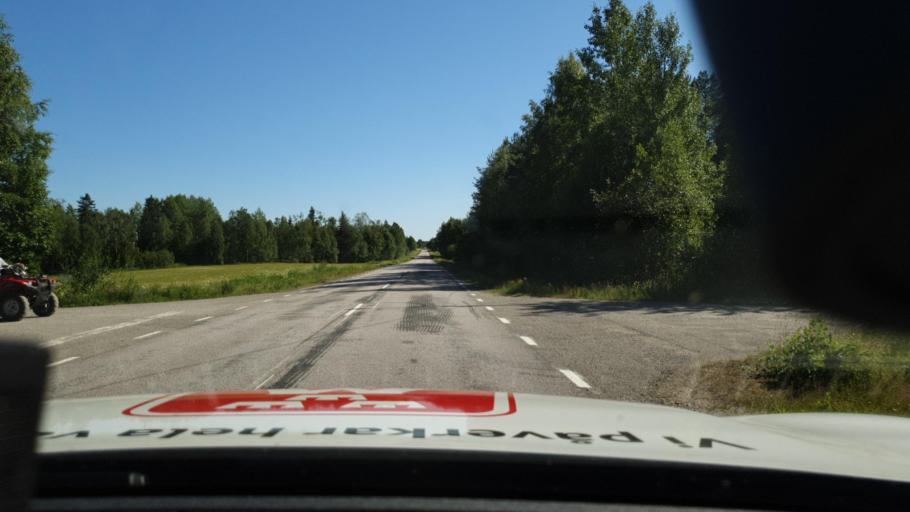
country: SE
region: Norrbotten
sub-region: Lulea Kommun
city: Ranea
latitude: 65.9115
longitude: 22.4514
